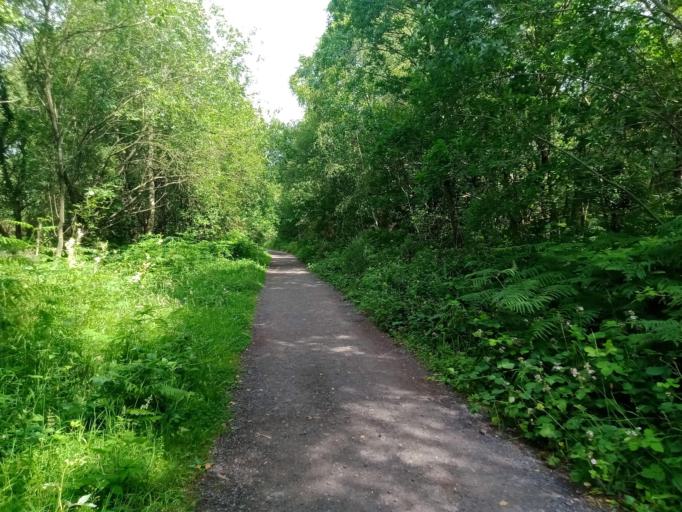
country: IE
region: Leinster
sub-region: Laois
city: Abbeyleix
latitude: 52.8994
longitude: -7.3501
